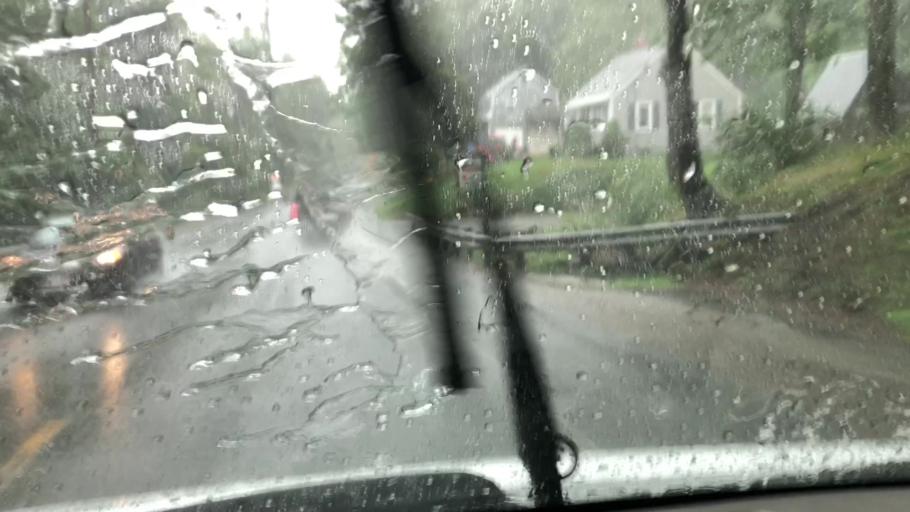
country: US
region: Massachusetts
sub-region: Hampshire County
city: Williamsburg
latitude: 42.4151
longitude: -72.7619
